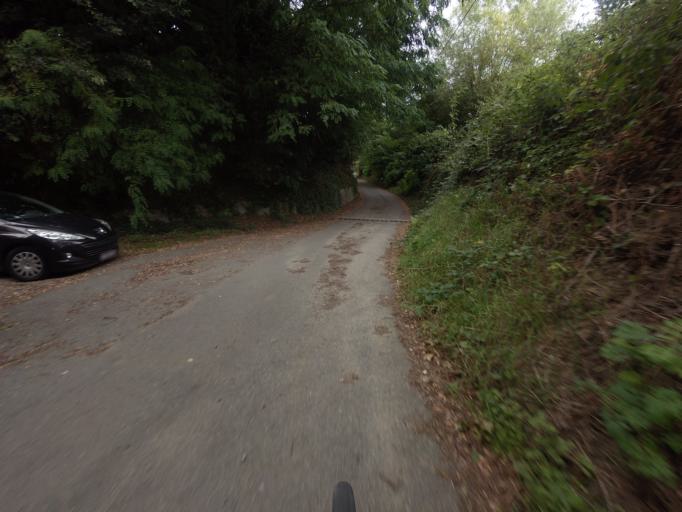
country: BE
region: Flanders
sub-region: Provincie Vlaams-Brabant
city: Leuven
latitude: 50.9010
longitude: 4.6958
